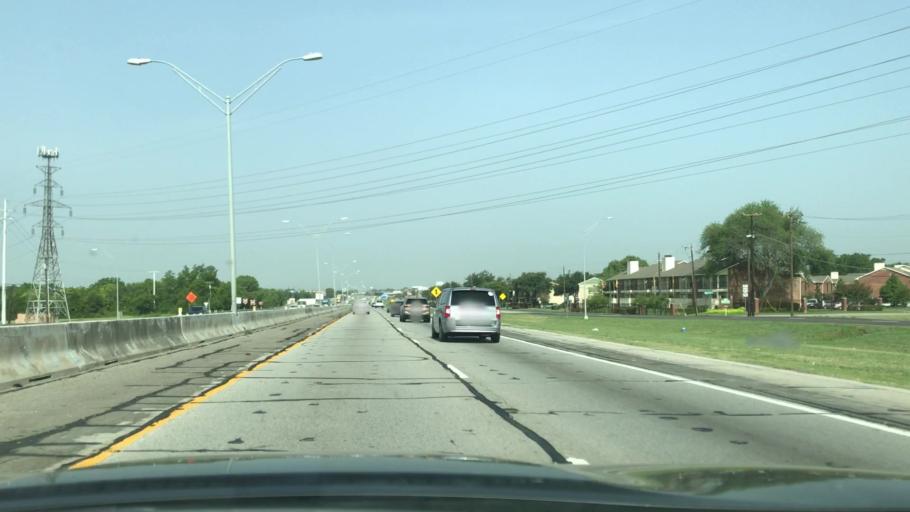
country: US
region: Texas
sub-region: Dallas County
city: Mesquite
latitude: 32.7925
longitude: -96.6370
